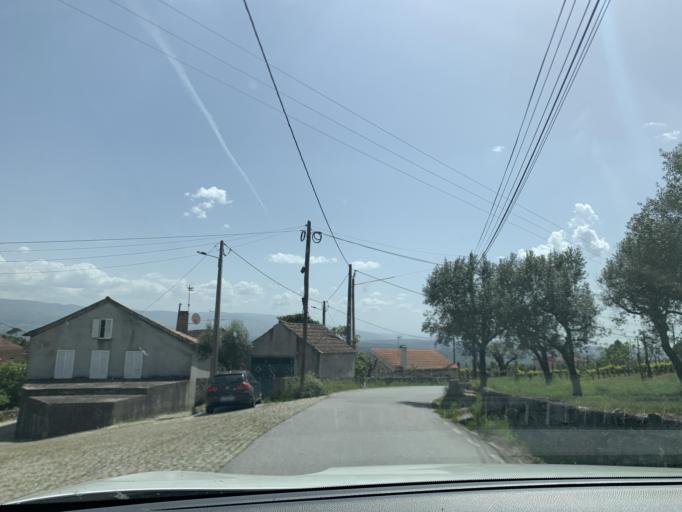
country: PT
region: Guarda
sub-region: Fornos de Algodres
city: Fornos de Algodres
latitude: 40.5914
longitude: -7.6291
